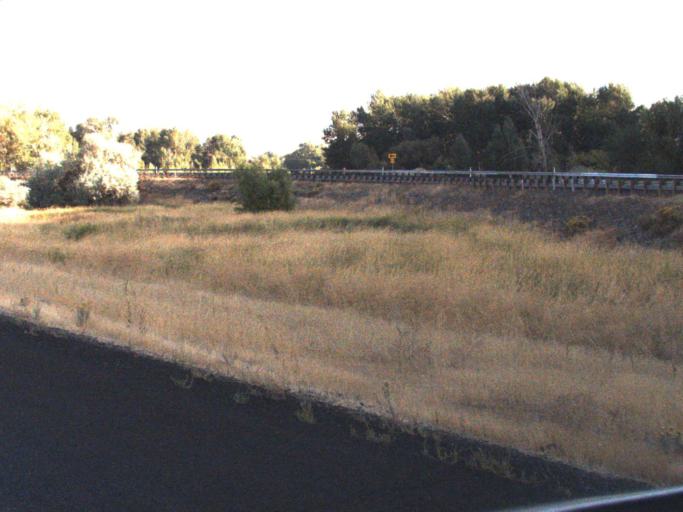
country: US
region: Washington
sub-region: Yakima County
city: Union Gap
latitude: 46.5337
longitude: -120.4716
